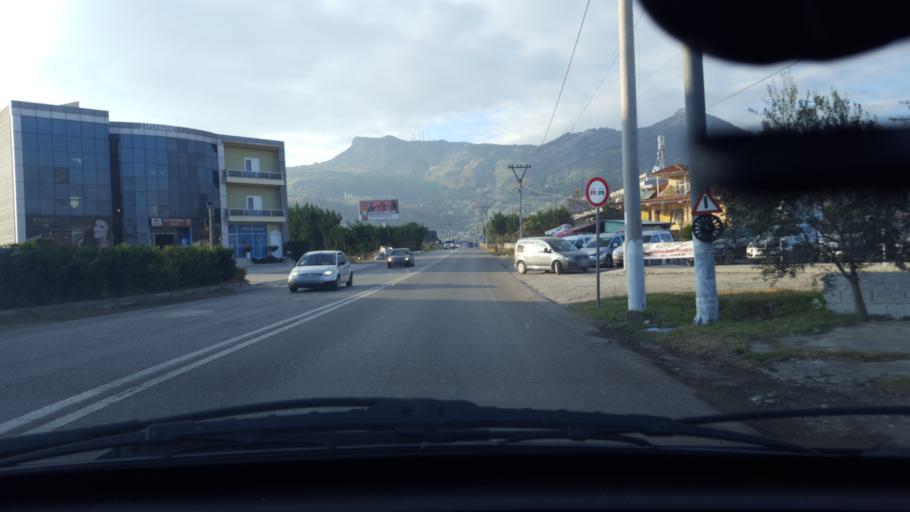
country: AL
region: Elbasan
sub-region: Rrethi i Elbasanit
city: Bradashesh
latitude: 41.0991
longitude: 20.0335
